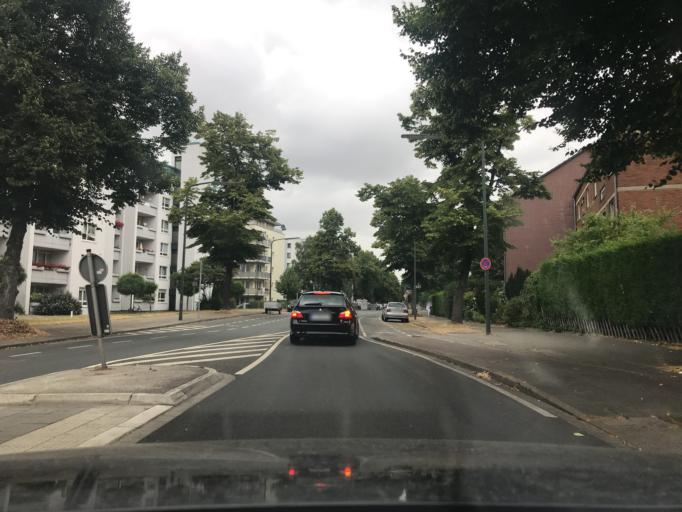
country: DE
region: North Rhine-Westphalia
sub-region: Regierungsbezirk Dusseldorf
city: Erkrath
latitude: 51.1827
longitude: 6.8667
